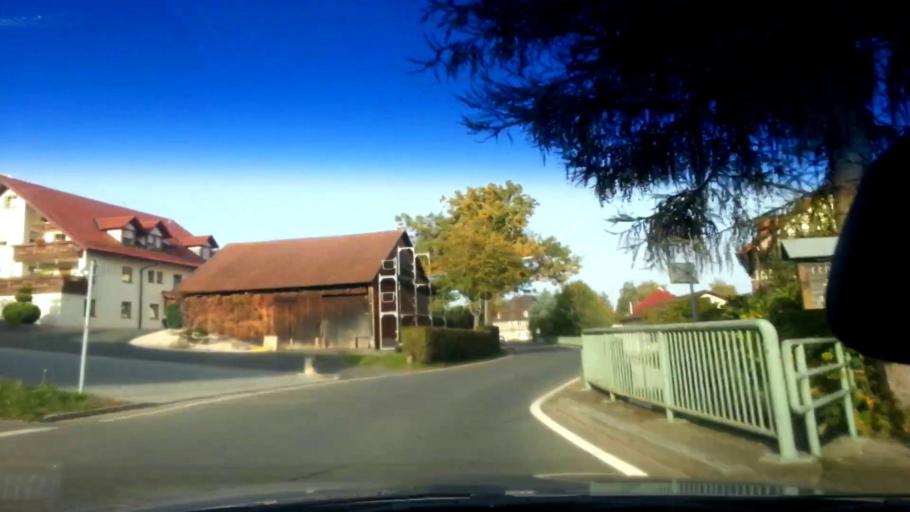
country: DE
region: Bavaria
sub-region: Upper Franconia
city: Schesslitz
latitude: 49.9782
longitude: 11.0297
